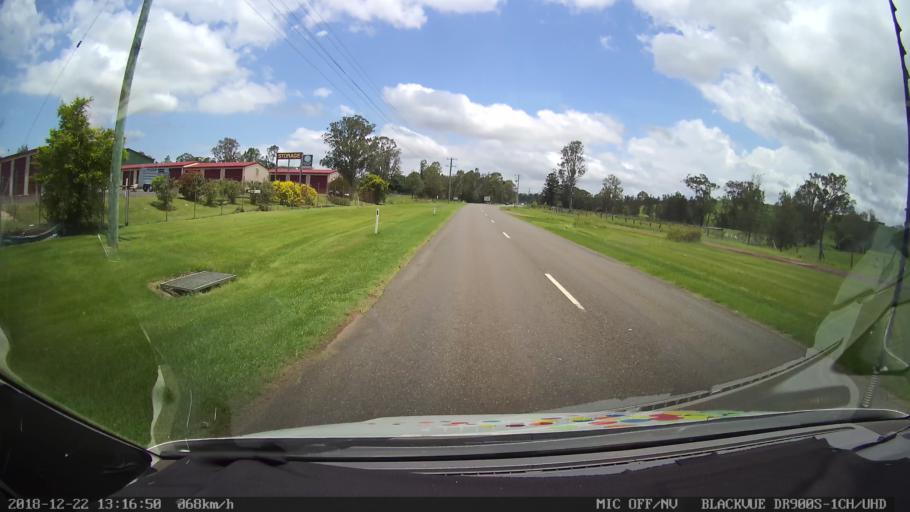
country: AU
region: New South Wales
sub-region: Clarence Valley
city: South Grafton
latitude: -29.7302
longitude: 152.9399
